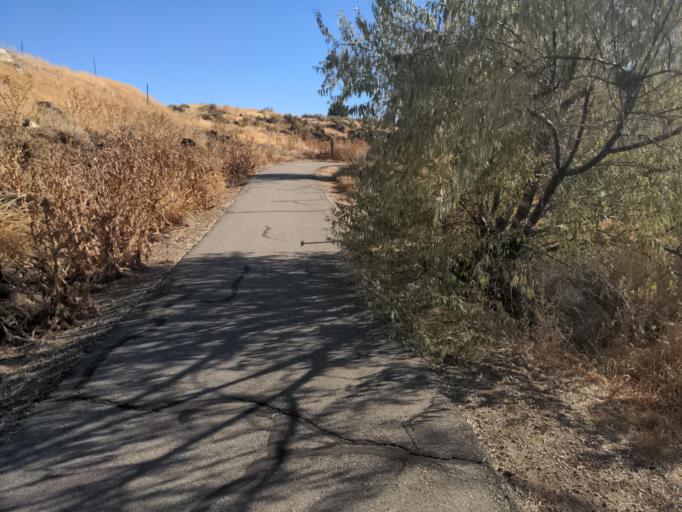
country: US
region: Idaho
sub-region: Elmore County
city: Mountain Home
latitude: 43.1455
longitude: -115.6722
